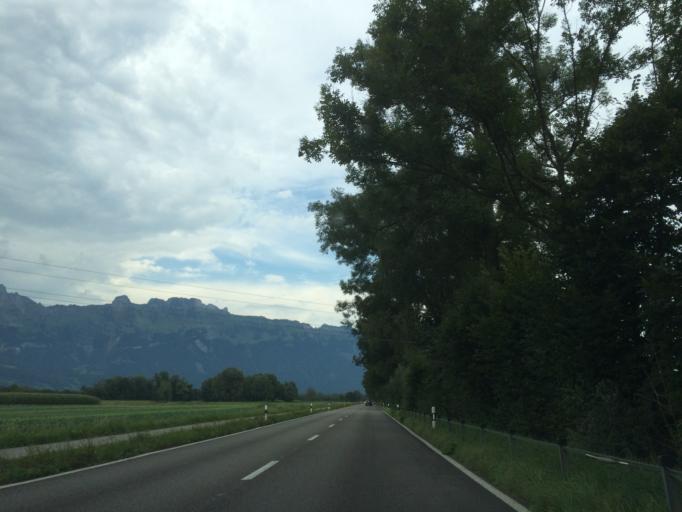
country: LI
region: Schaan
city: Schaan
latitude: 47.1858
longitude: 9.5056
